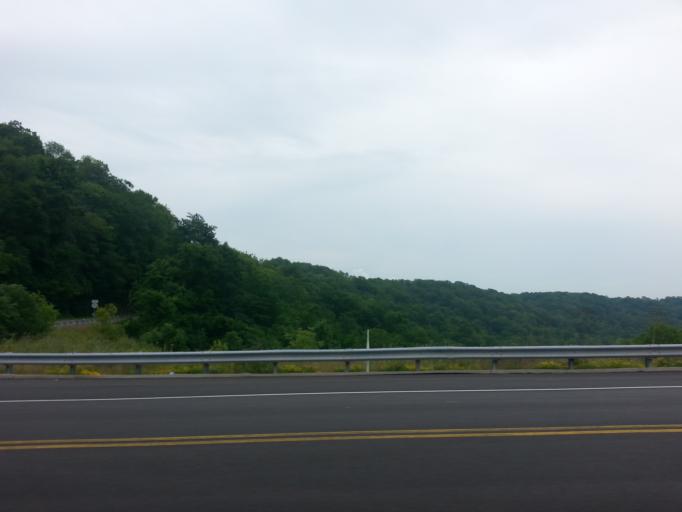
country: US
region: Ohio
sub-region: Brown County
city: Aberdeen
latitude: 38.6733
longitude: -83.7981
